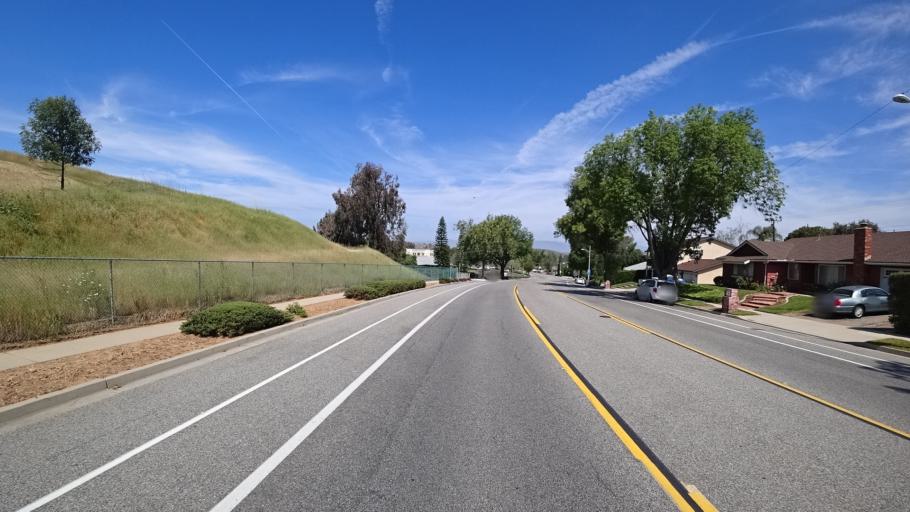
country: US
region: California
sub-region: Ventura County
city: Thousand Oaks
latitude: 34.2021
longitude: -118.8755
